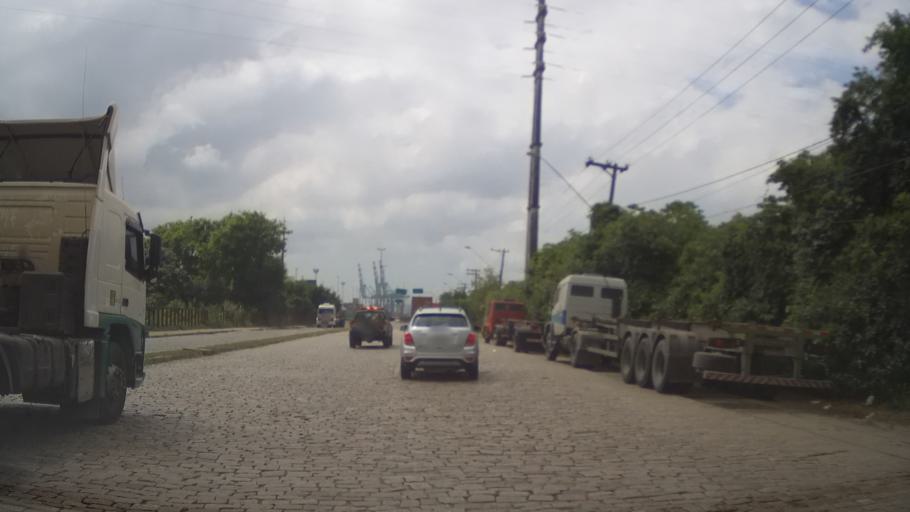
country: BR
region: Sao Paulo
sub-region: Santos
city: Santos
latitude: -23.9265
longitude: -46.3493
